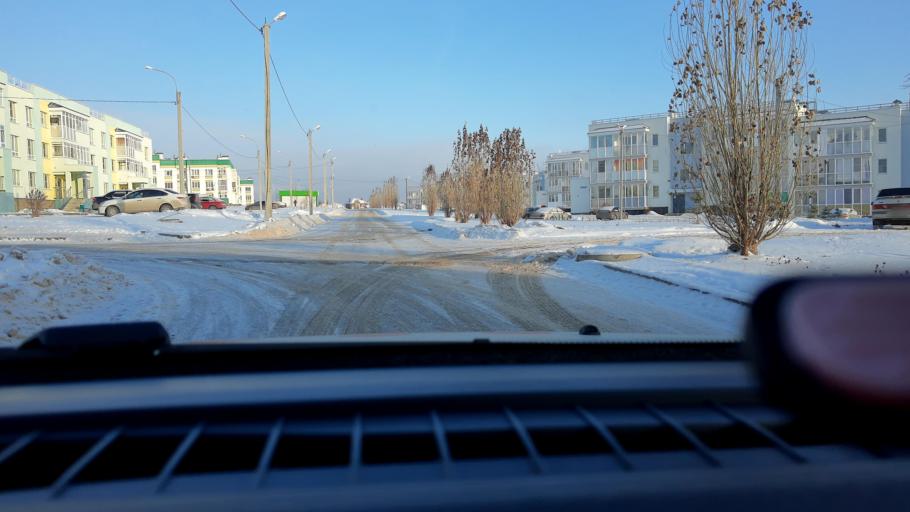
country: RU
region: Nizjnij Novgorod
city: Burevestnik
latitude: 56.1896
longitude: 43.8602
